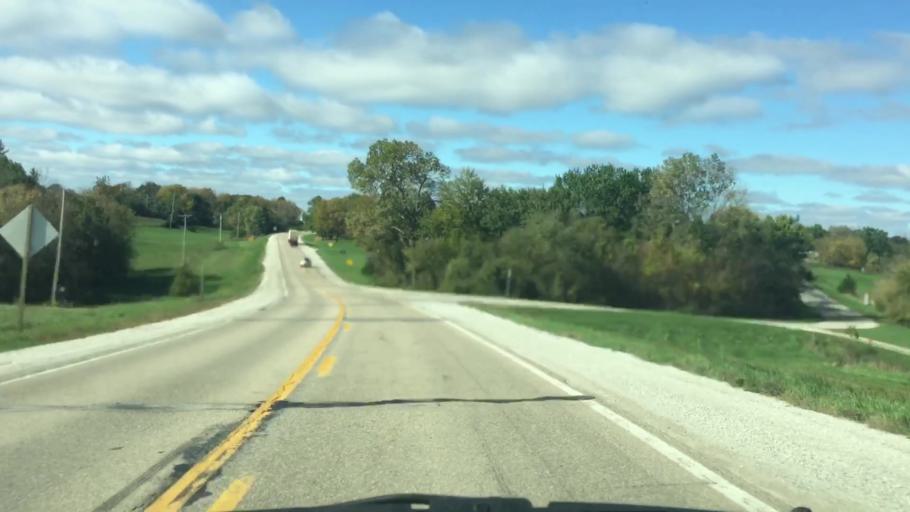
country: US
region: Iowa
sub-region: Decatur County
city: Leon
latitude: 40.7415
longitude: -93.8244
